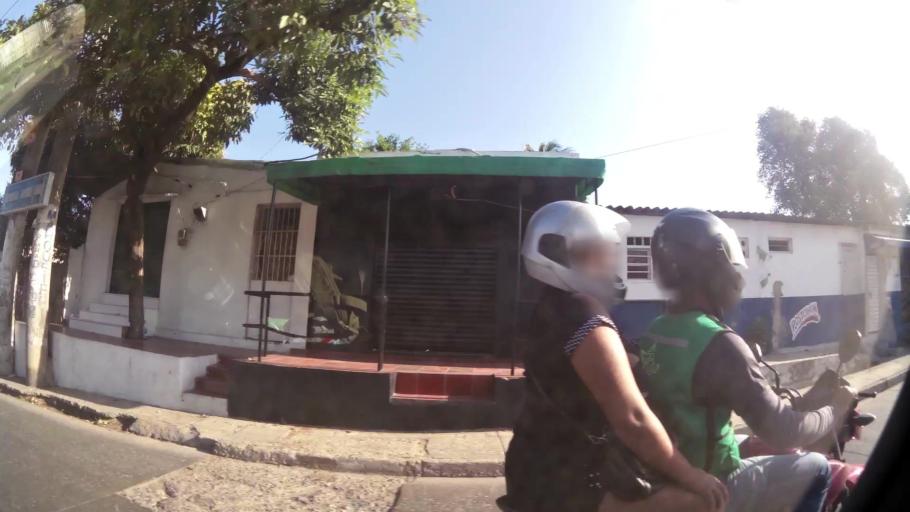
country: CO
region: Bolivar
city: Cartagena
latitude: 10.3990
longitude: -75.4992
